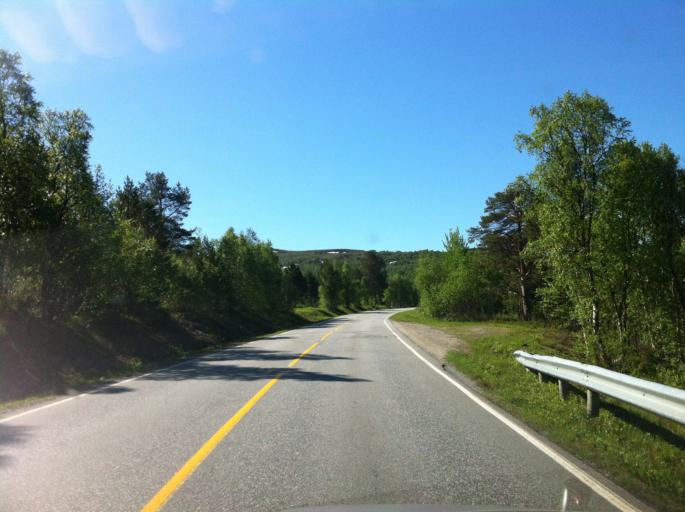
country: NO
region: Sor-Trondelag
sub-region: Roros
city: Roros
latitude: 62.6102
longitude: 11.8464
